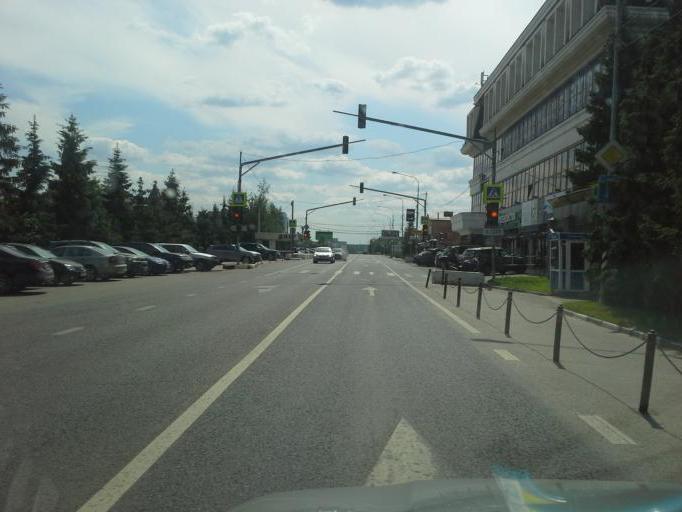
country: RU
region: Moskovskaya
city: Gorki Vtoryye
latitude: 55.7064
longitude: 37.1615
